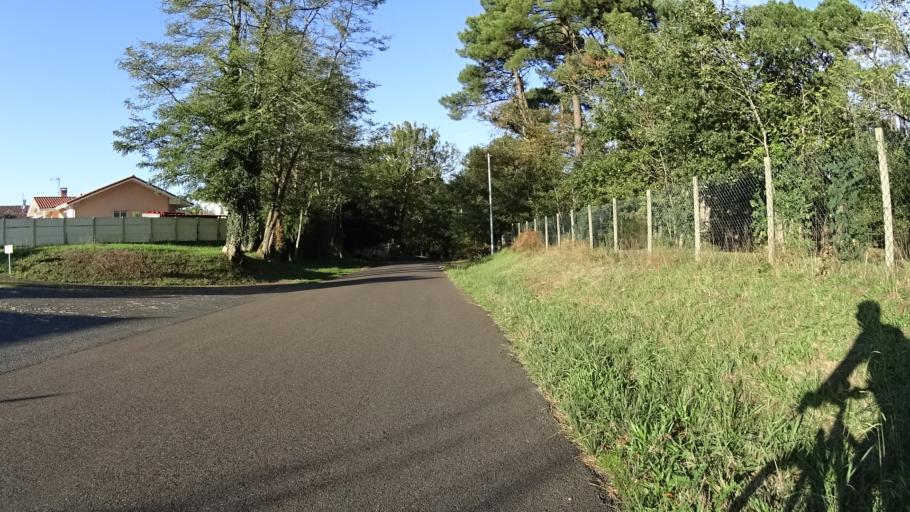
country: FR
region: Aquitaine
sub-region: Departement des Landes
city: Saint-Paul-les-Dax
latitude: 43.7345
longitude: -1.0441
